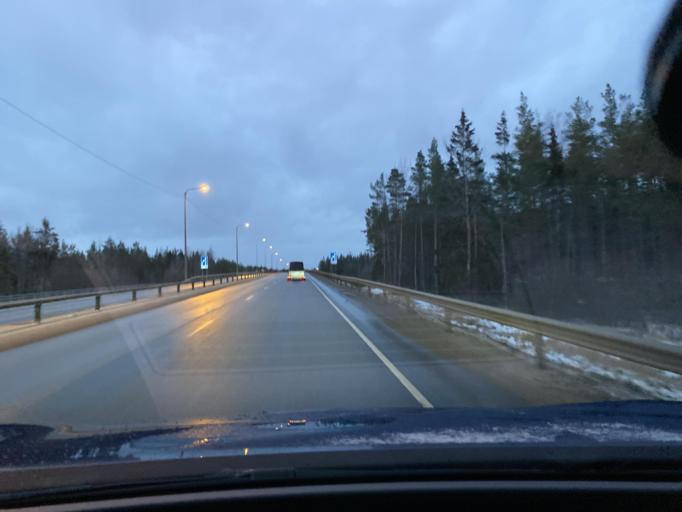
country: FI
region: Satakunta
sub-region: Rauma
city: Rauma
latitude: 61.1414
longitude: 21.5491
